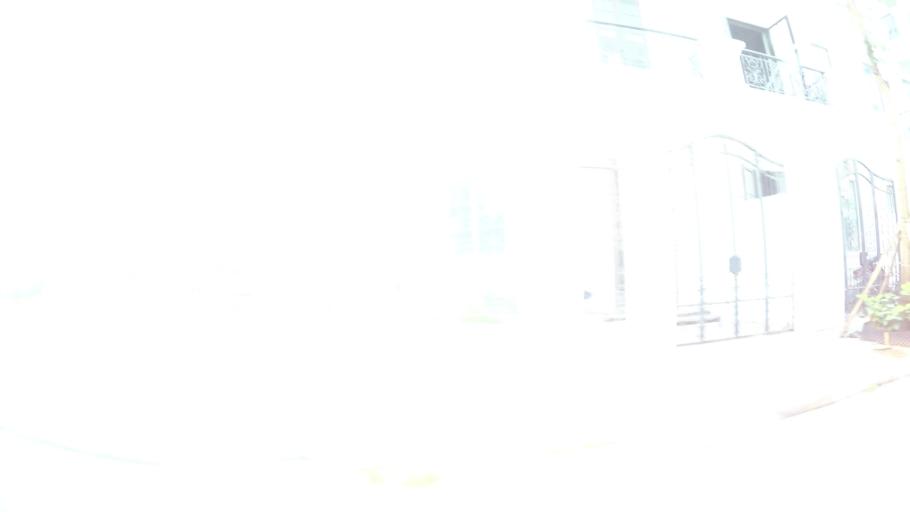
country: VN
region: Ha Noi
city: Thanh Xuan
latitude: 20.9752
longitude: 105.8187
